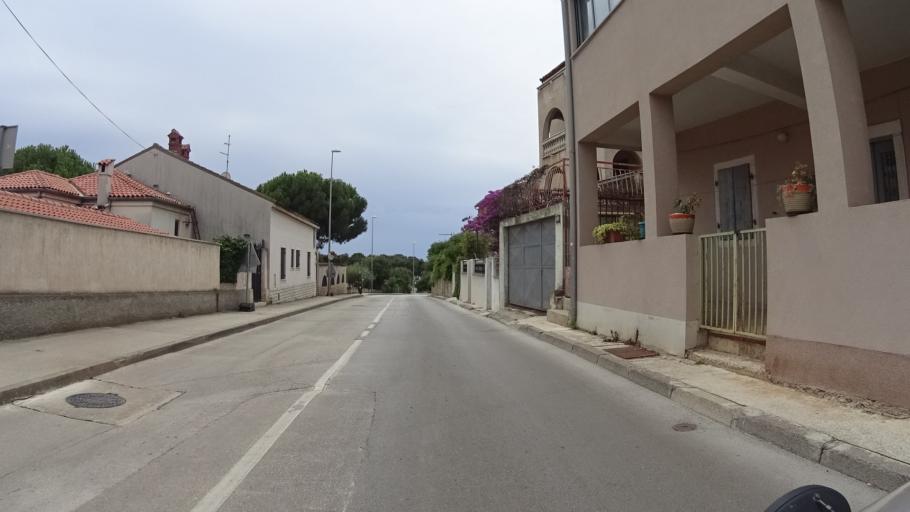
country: HR
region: Istarska
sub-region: Grad Pula
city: Pula
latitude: 44.8619
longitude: 13.8183
